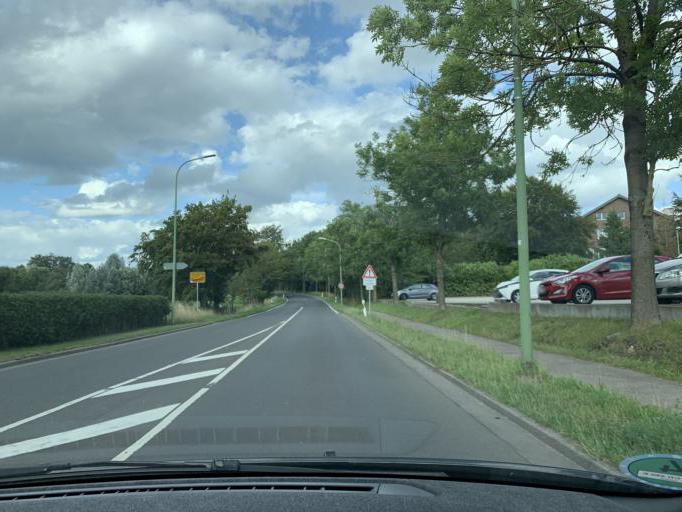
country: DE
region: North Rhine-Westphalia
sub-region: Regierungsbezirk Koln
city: Simmerath
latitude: 50.6103
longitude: 6.3062
